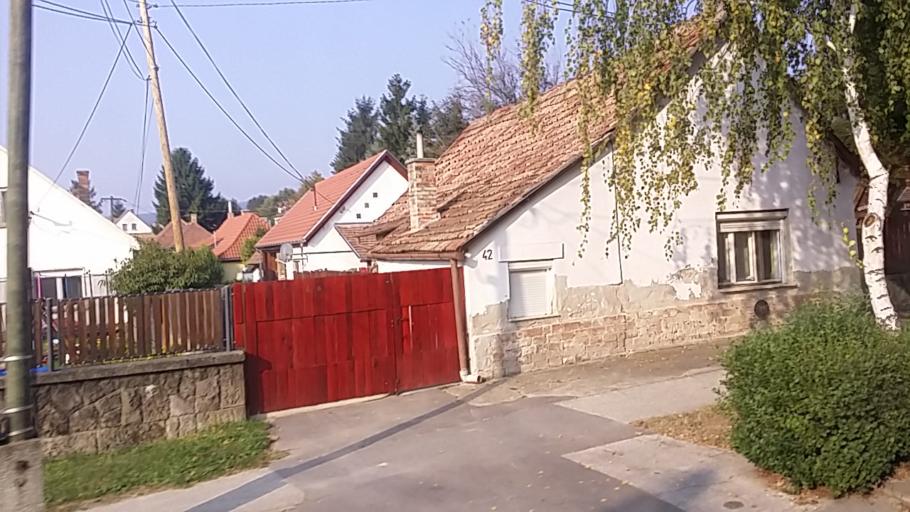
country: HU
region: Pest
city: Pilisszanto
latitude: 47.6676
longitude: 18.8882
